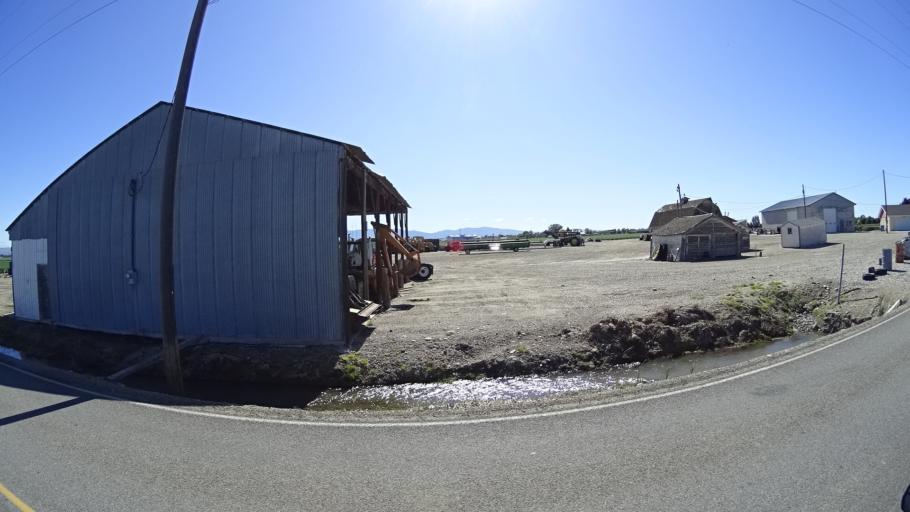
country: US
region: Idaho
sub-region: Ada County
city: Star
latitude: 43.6390
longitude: -116.4536
